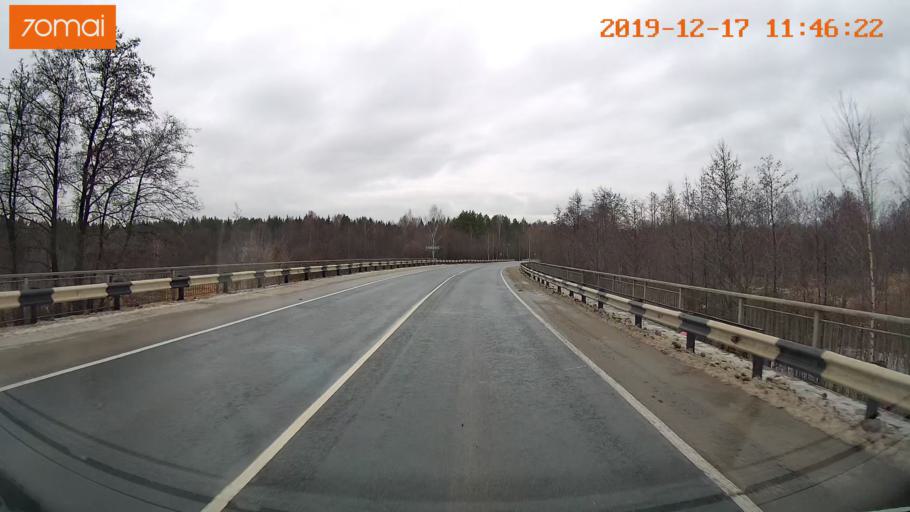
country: RU
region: Vladimir
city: Velikodvorskiy
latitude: 55.2428
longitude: 40.6755
